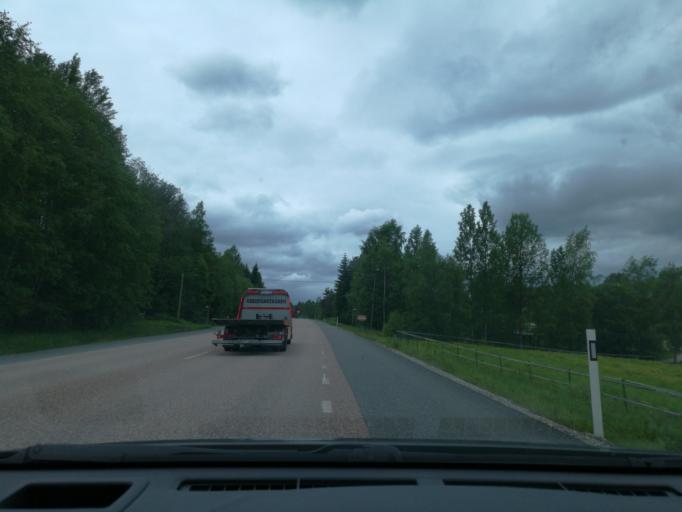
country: SE
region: Vaestmanland
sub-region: Fagersta Kommun
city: Fagersta
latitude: 59.9716
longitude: 15.7154
